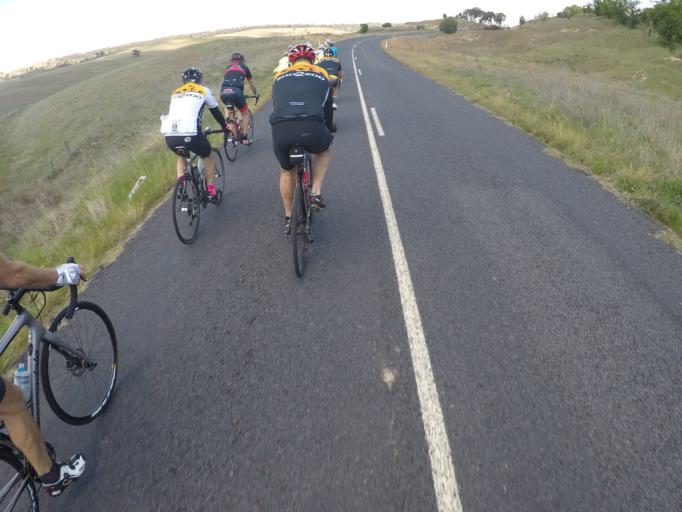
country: AU
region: New South Wales
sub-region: Blayney
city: Blayney
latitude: -33.5772
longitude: 149.4046
